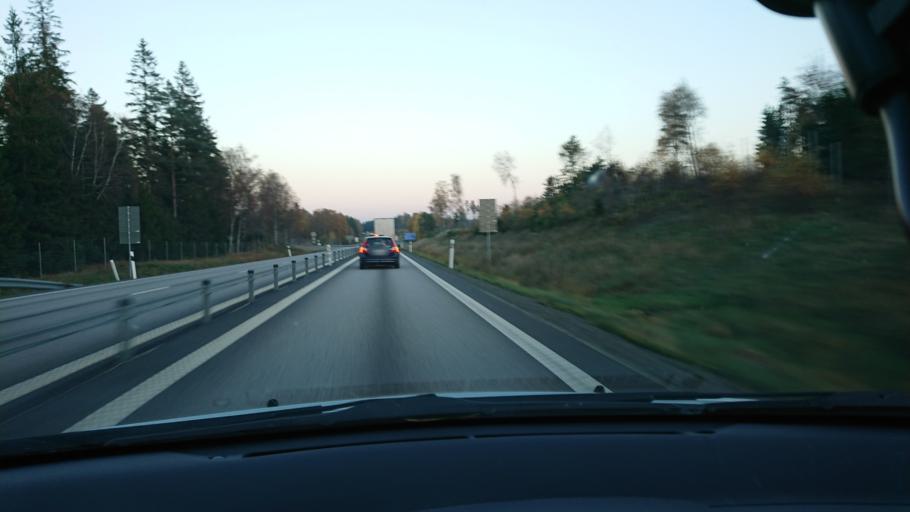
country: SE
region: Halland
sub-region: Laholms Kommun
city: Knared
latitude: 56.7248
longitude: 13.3651
